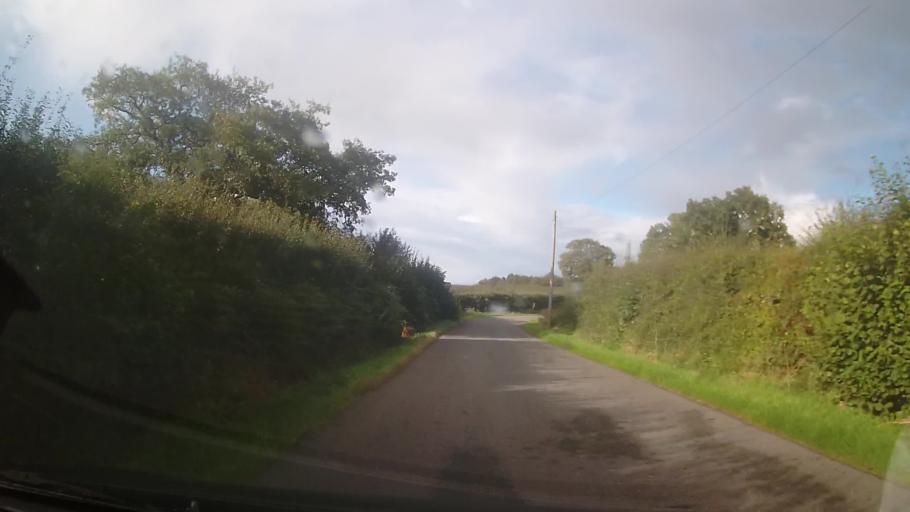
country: GB
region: England
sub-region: Shropshire
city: Whitchurch
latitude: 52.9262
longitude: -2.7304
